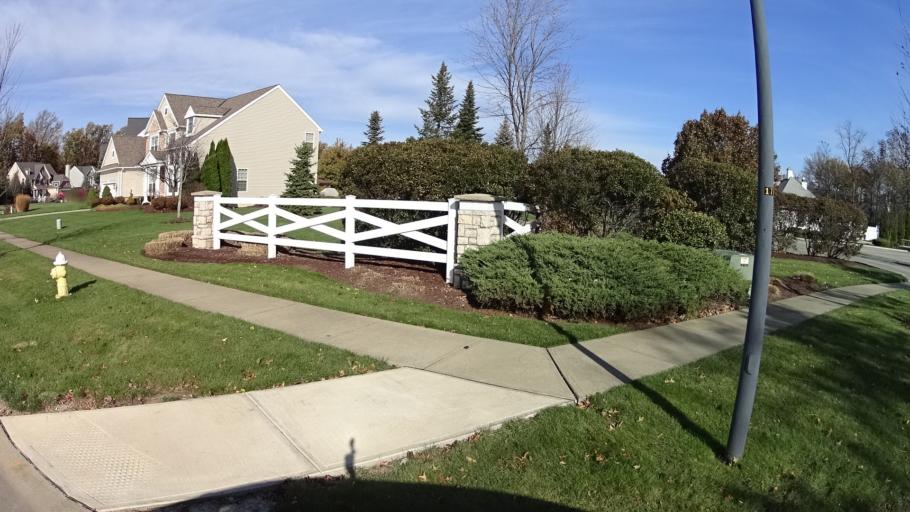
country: US
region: Ohio
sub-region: Lorain County
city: Avon Lake
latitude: 41.4941
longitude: -82.0398
